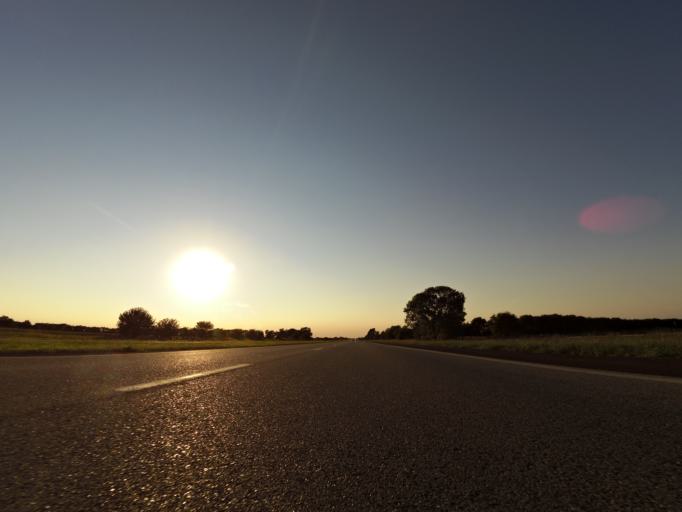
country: US
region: Kansas
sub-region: Reno County
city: Haven
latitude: 37.9177
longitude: -97.8244
